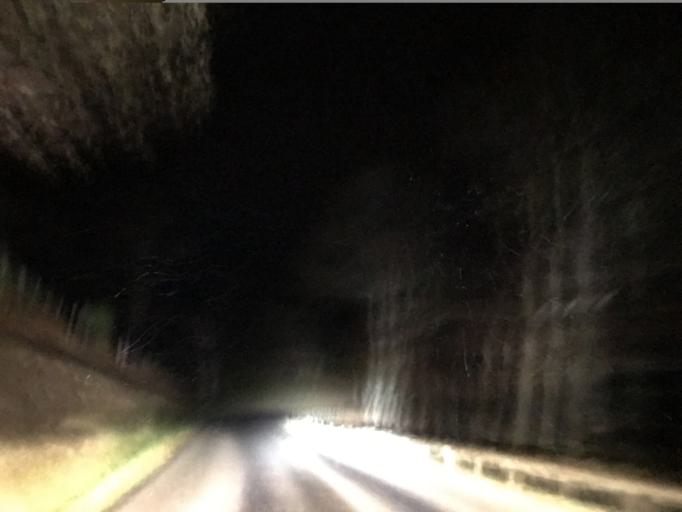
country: FR
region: Auvergne
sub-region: Departement du Puy-de-Dome
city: Saint-Remy-sur-Durolle
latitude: 45.9032
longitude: 3.6295
